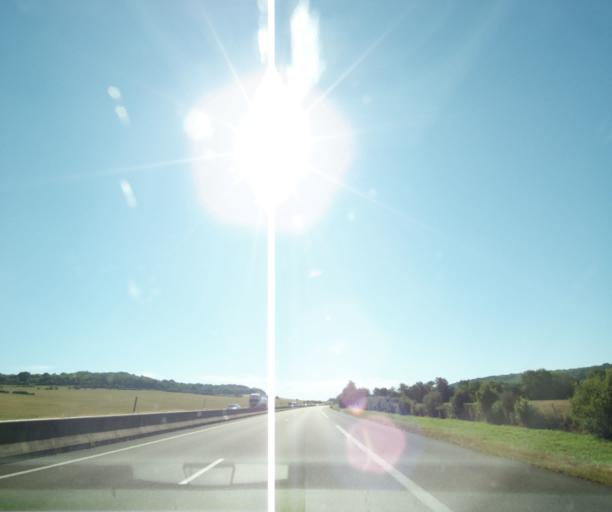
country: FR
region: Champagne-Ardenne
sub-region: Departement de la Haute-Marne
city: Nogent-le-Bas
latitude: 47.9572
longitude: 5.4089
